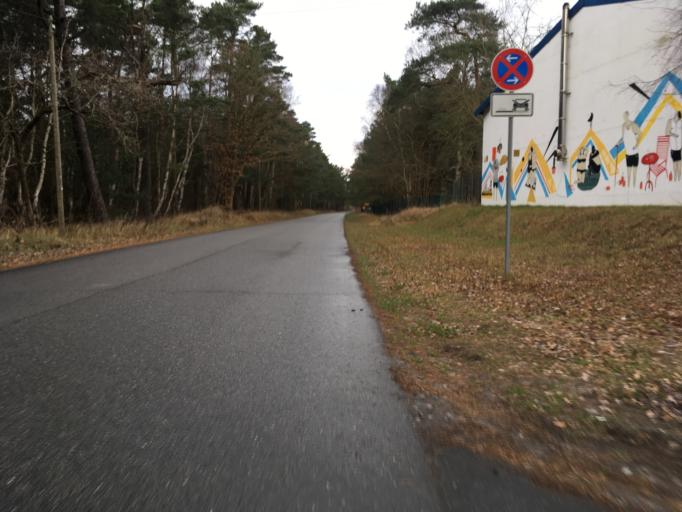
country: DE
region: Mecklenburg-Vorpommern
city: Ostseebad Binz
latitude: 54.4506
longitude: 13.5649
